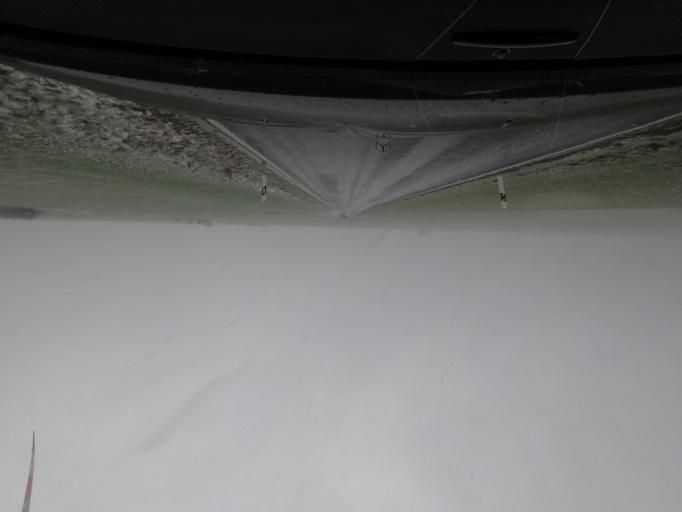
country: DE
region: Thuringia
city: Buttstedt
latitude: 51.2585
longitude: 10.2771
